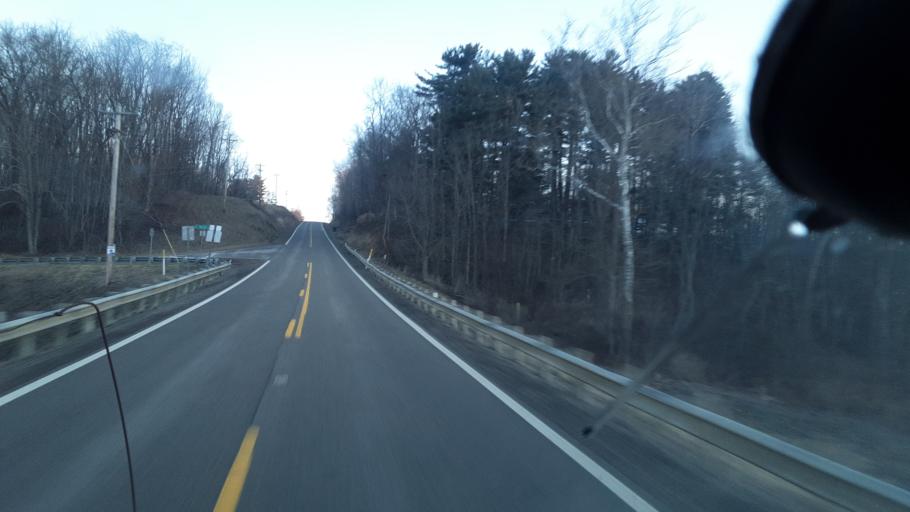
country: US
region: Ohio
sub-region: Perry County
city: Somerset
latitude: 39.7667
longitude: -82.3035
